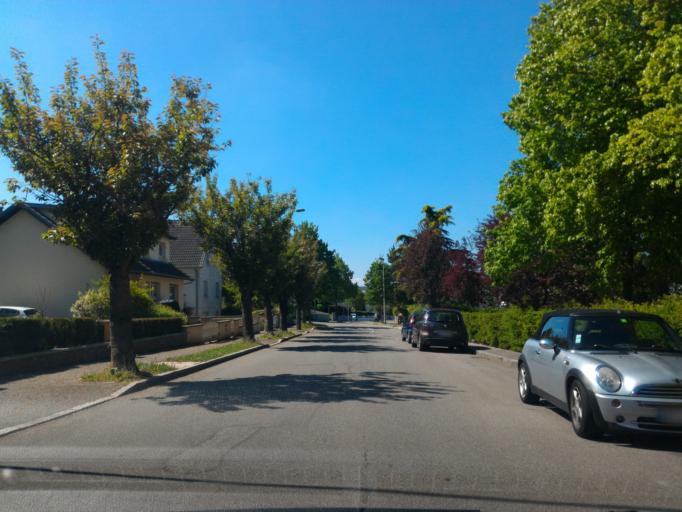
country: FR
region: Alsace
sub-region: Departement du Haut-Rhin
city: Riedisheim
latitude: 47.7516
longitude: 7.3731
